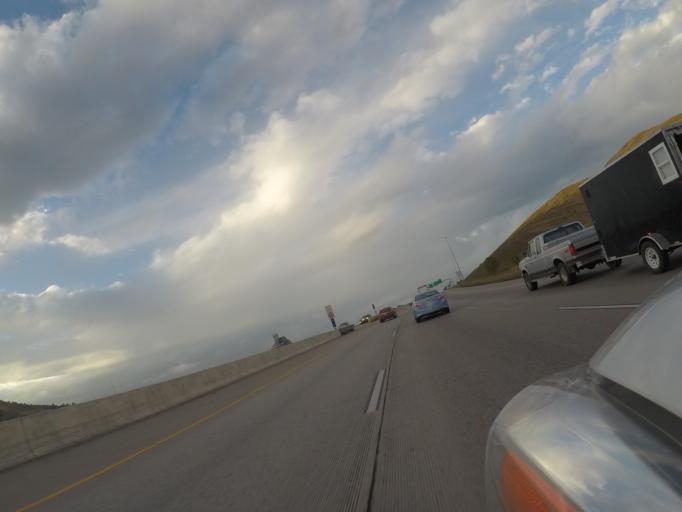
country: US
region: Colorado
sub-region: Jefferson County
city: West Pleasant View
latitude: 39.7016
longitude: -105.1936
